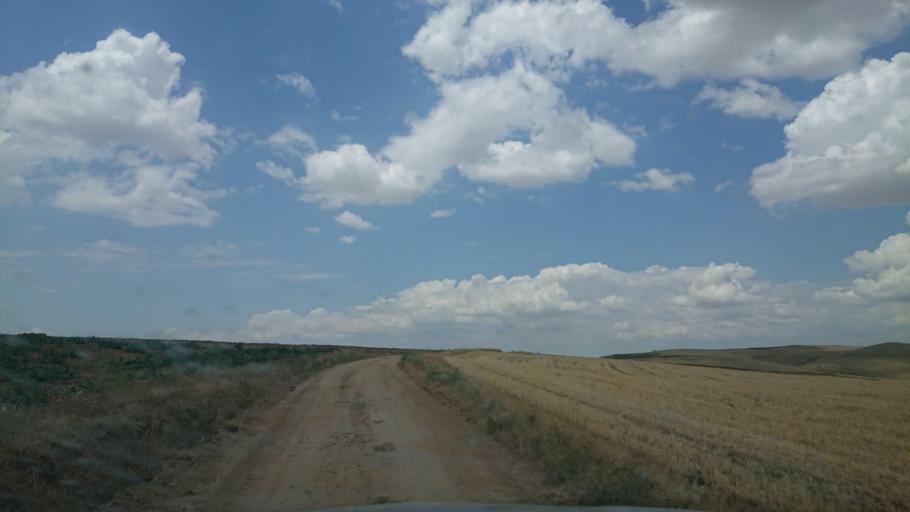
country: TR
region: Aksaray
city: Agacoren
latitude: 38.8975
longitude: 33.8831
